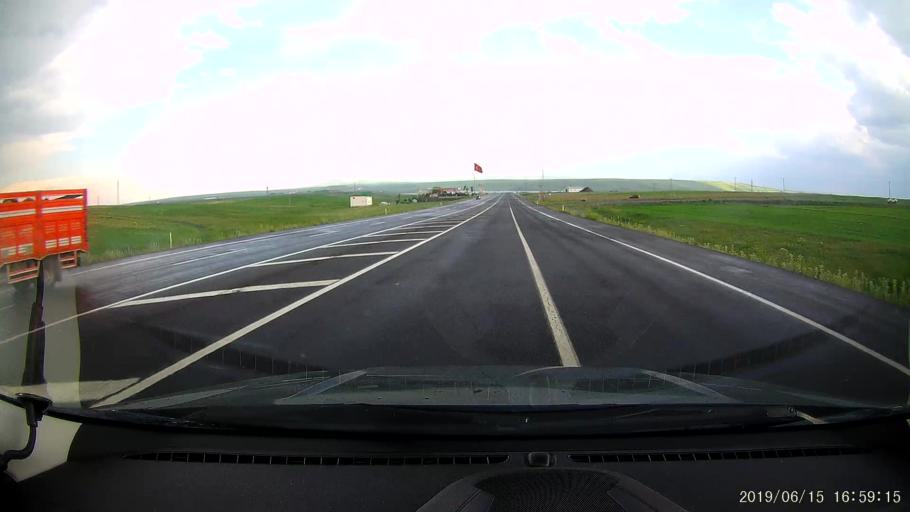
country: TR
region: Kars
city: Susuz
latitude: 40.7544
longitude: 43.1493
